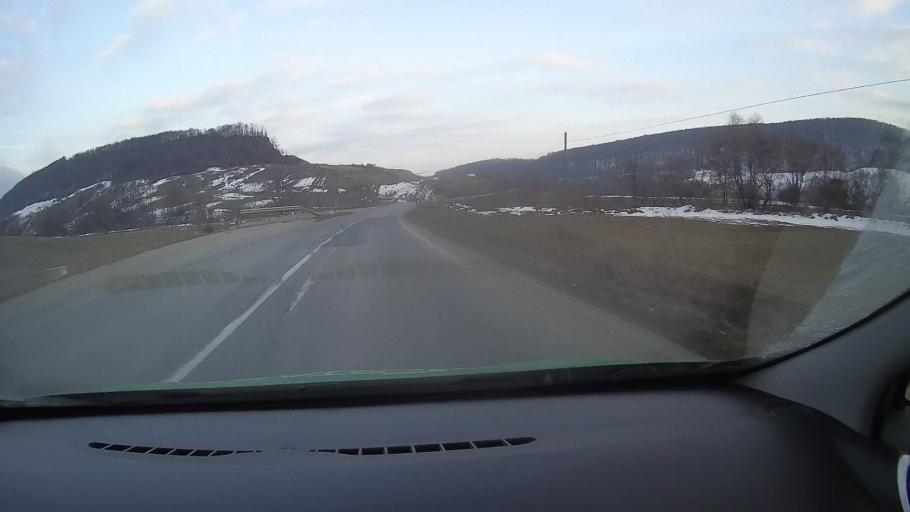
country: RO
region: Harghita
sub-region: Comuna Lupeni
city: Lupeni
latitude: 46.3605
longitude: 25.1870
